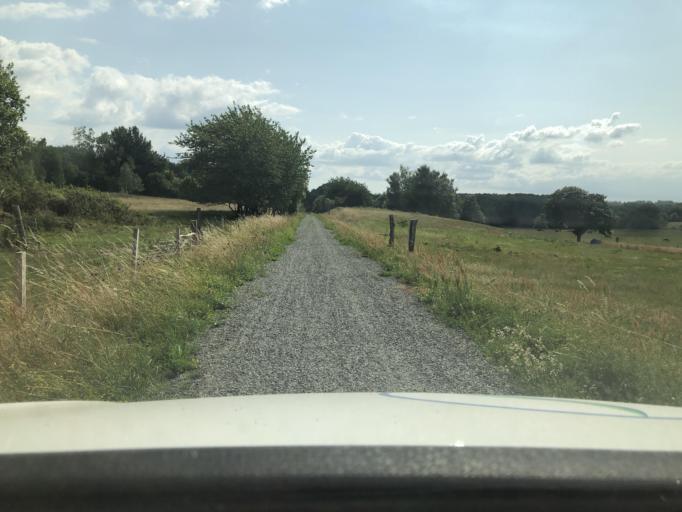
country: SE
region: Skane
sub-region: Kristianstads Kommun
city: Degeberga
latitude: 55.7650
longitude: 14.1493
